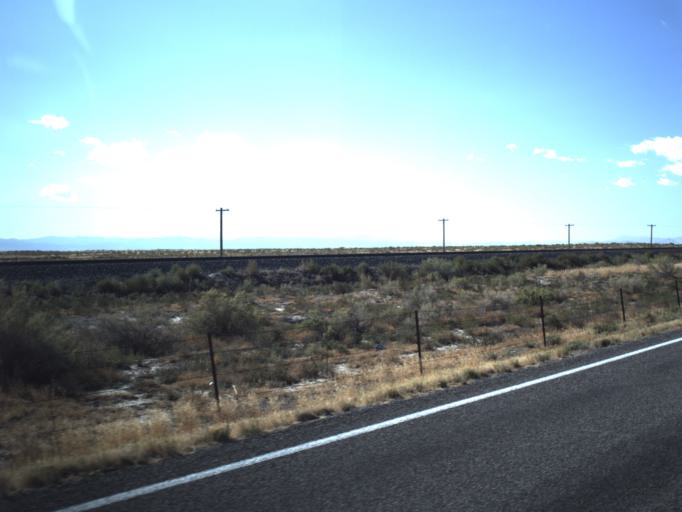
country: US
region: Utah
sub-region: Millard County
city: Delta
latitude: 39.2134
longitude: -112.6797
